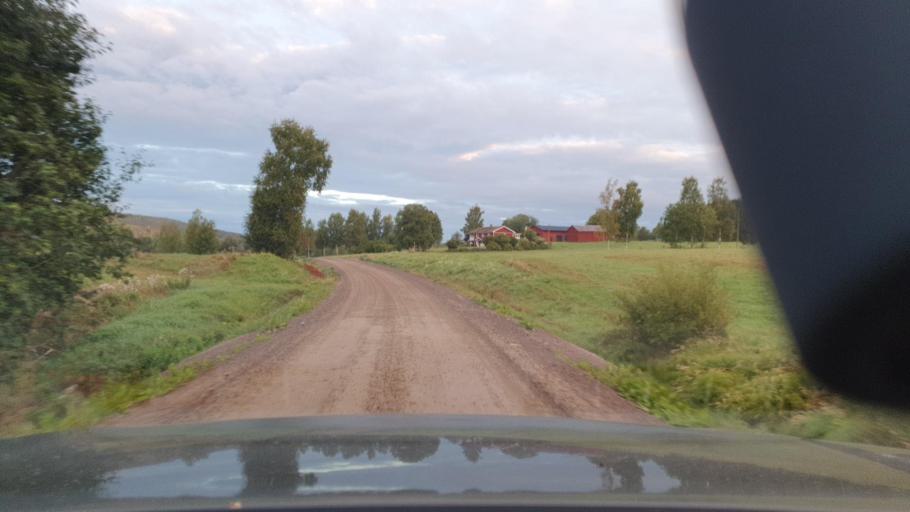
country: SE
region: Vaermland
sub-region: Sunne Kommun
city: Sunne
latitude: 59.8159
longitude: 13.0491
